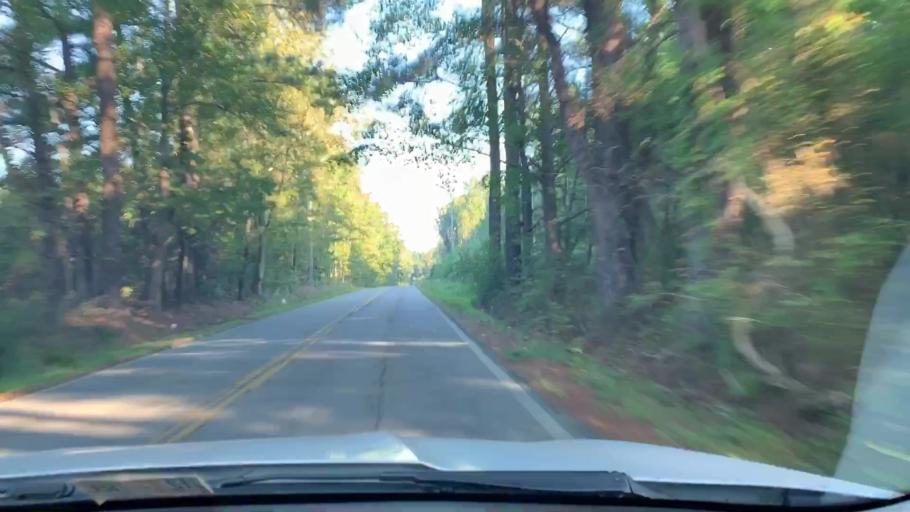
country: US
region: Virginia
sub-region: Middlesex County
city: Deltaville
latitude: 37.5627
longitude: -76.4512
